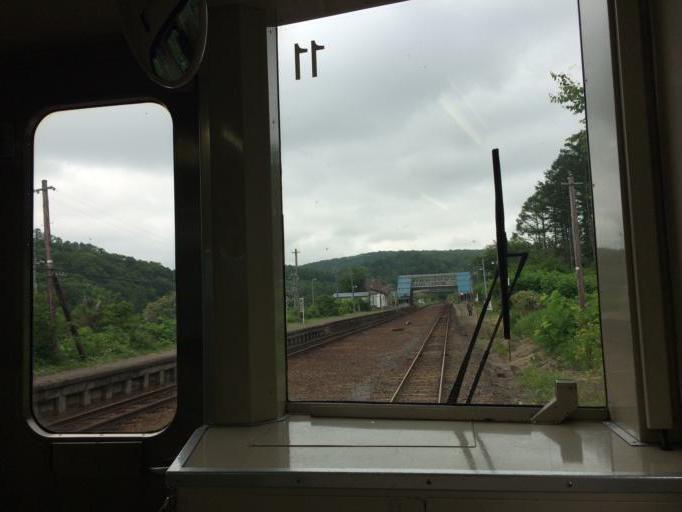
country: JP
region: Hokkaido
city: Otaru
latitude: 43.2023
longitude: 140.9233
